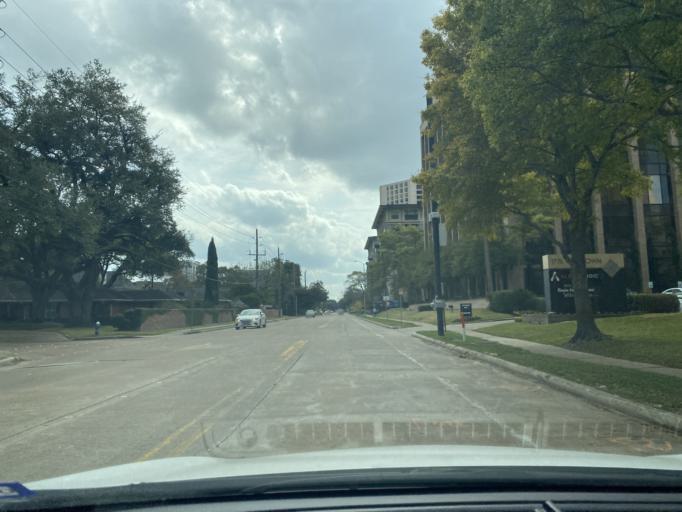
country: US
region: Texas
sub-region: Harris County
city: Hunters Creek Village
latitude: 29.7482
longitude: -95.4709
